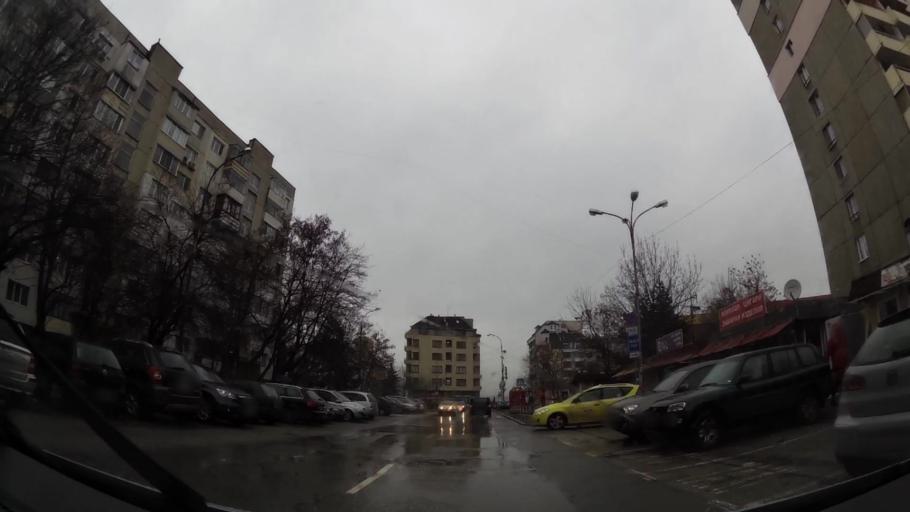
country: BG
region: Sofia-Capital
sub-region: Stolichna Obshtina
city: Sofia
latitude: 42.6423
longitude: 23.3677
